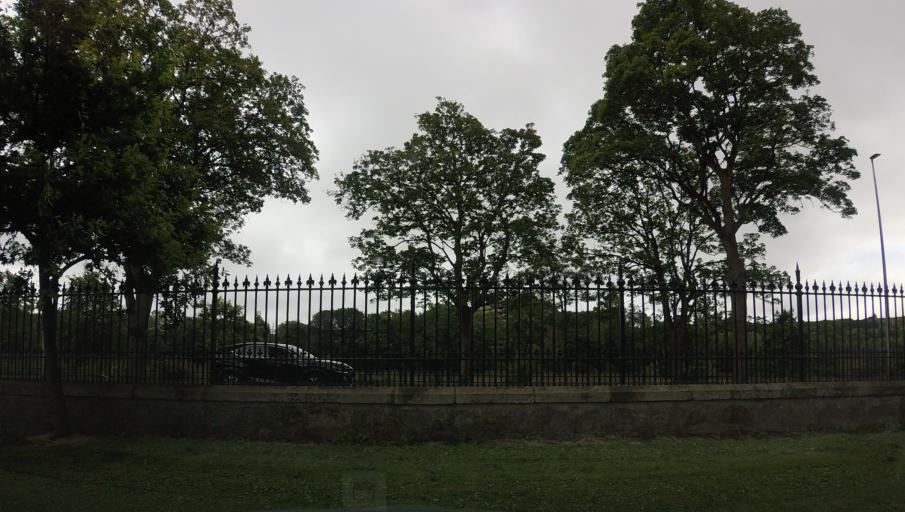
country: GB
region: Scotland
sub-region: Aberdeen City
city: Aberdeen
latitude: 57.1296
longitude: -2.0994
